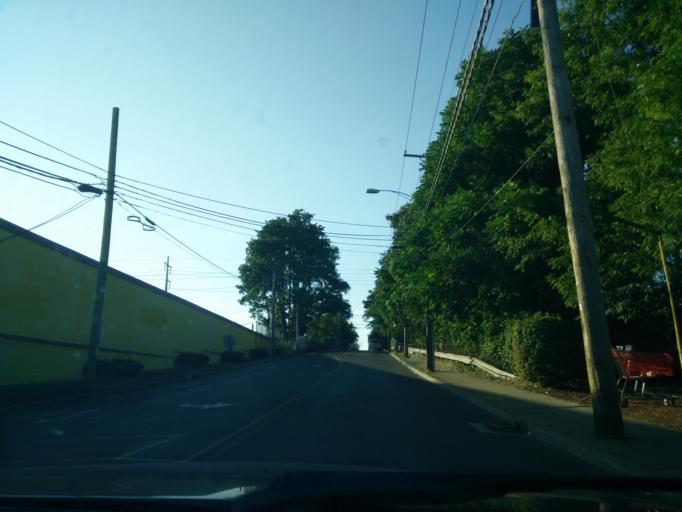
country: US
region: Connecticut
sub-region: Fairfield County
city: Bridgeport
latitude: 41.1618
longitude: -73.2312
